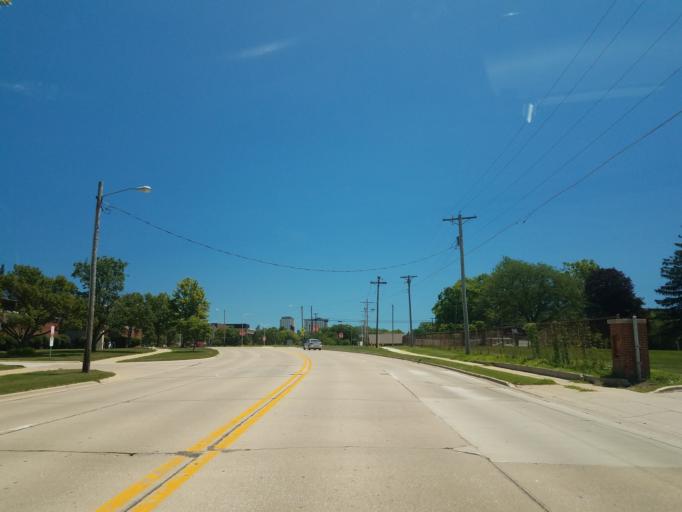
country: US
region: Illinois
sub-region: McLean County
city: Normal
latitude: 40.5099
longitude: -88.9978
